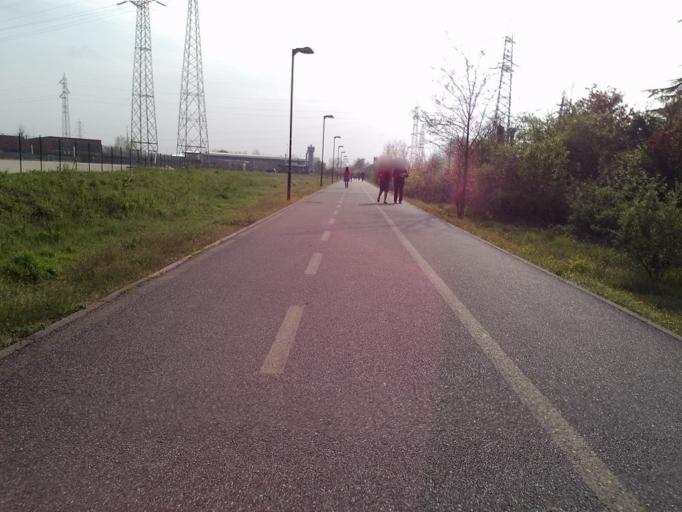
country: IT
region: Veneto
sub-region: Provincia di Verona
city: Verona
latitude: 45.4158
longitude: 10.9533
